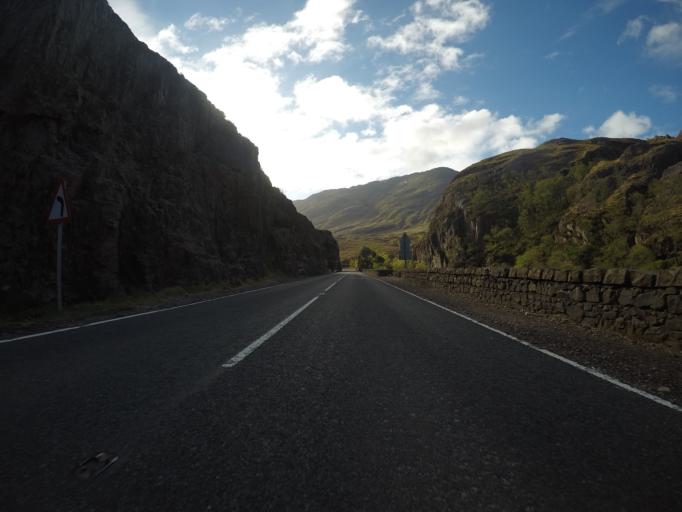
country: GB
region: Scotland
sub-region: Highland
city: Fort William
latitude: 56.6634
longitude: -4.9692
